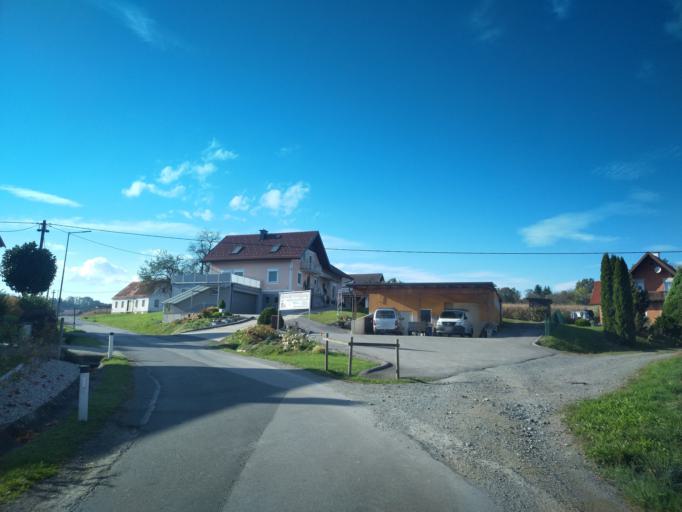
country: AT
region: Styria
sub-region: Politischer Bezirk Leibnitz
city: Sankt Johann im Saggautal
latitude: 46.7013
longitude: 15.3869
